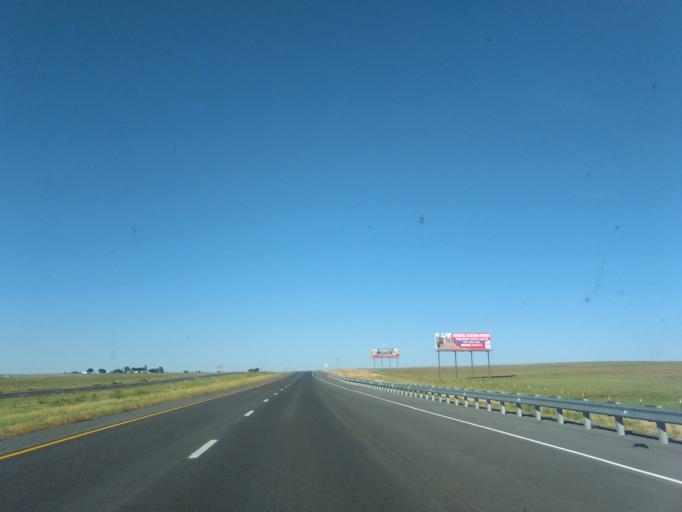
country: US
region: New Mexico
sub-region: San Miguel County
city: Las Vegas
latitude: 35.6800
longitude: -105.1648
